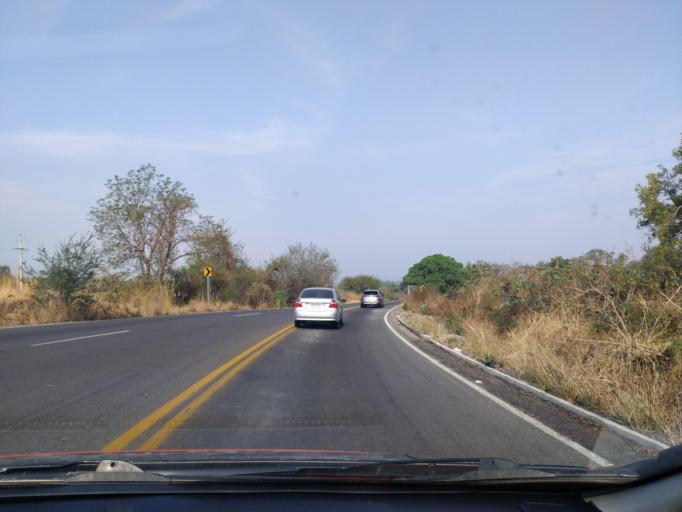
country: MX
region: Jalisco
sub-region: Acatlan de Juarez
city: Villa de los Ninos
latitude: 20.4166
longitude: -103.5793
